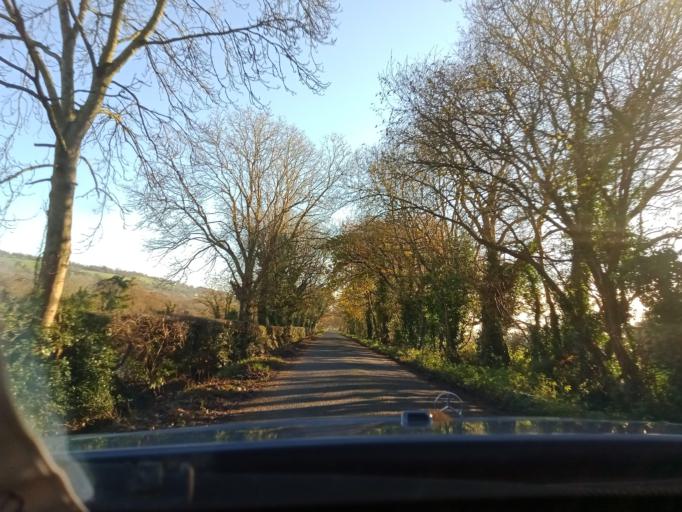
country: IE
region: Leinster
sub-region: Kilkenny
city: Piltown
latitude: 52.3537
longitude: -7.2931
